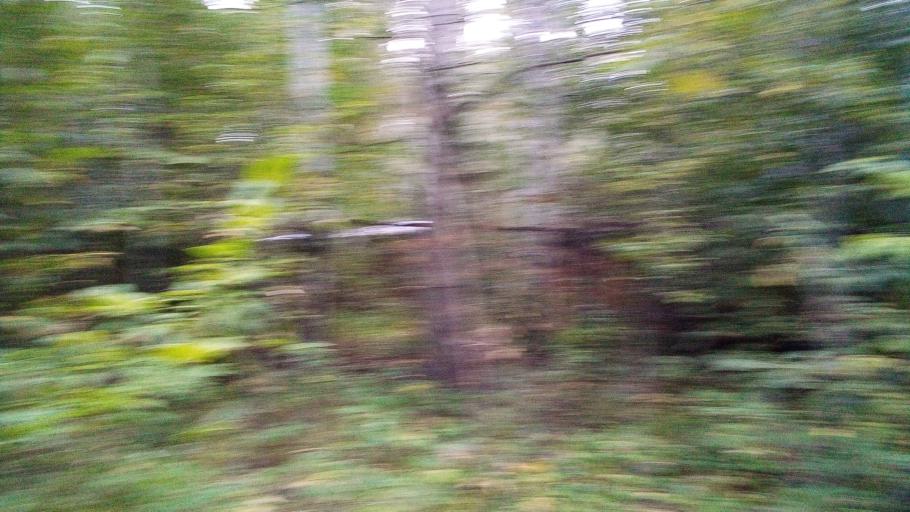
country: RU
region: Chelyabinsk
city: Tayginka
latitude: 55.4768
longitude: 60.5014
